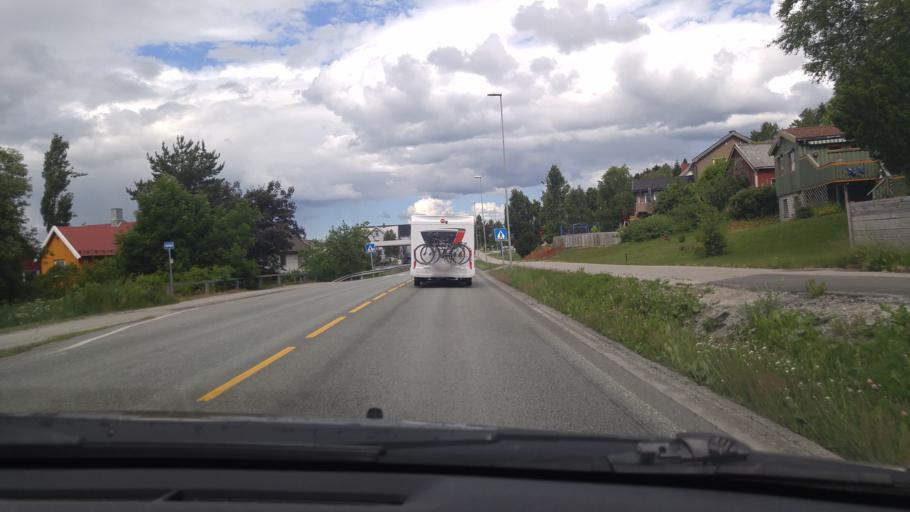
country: NO
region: Nord-Trondelag
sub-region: Steinkjer
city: Steinkjer
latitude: 63.9180
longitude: 11.4335
